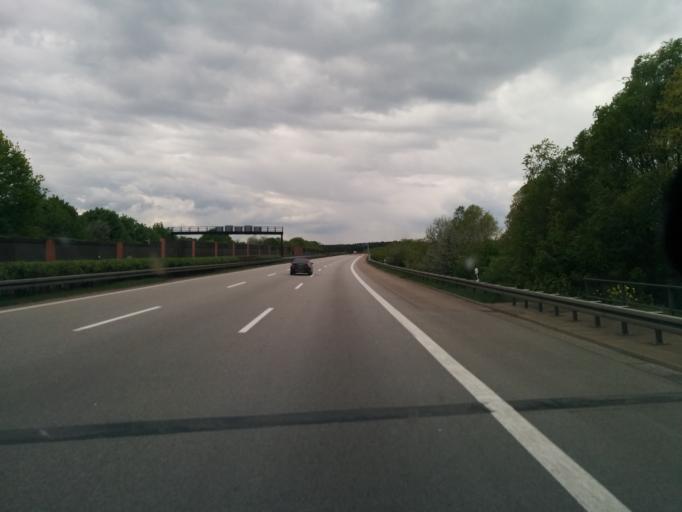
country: DE
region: Brandenburg
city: Gross Kreutz
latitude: 52.3400
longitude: 12.7255
